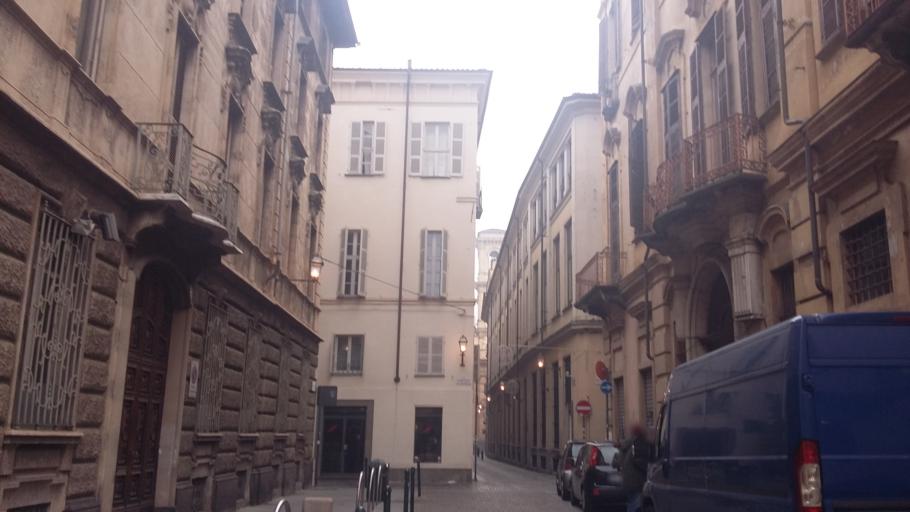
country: IT
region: Piedmont
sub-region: Provincia di Torino
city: Turin
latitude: 45.0725
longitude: 7.6790
